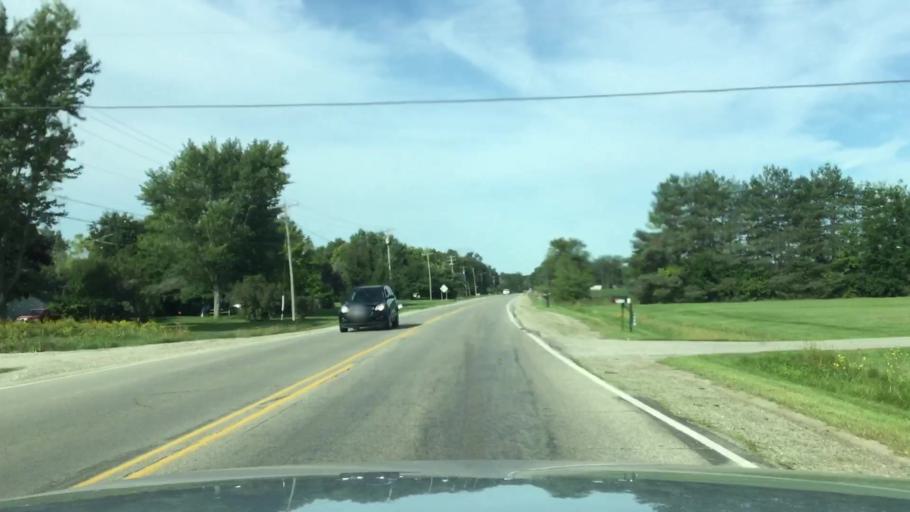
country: US
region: Michigan
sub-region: Genesee County
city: Flushing
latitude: 43.1181
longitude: -83.8149
